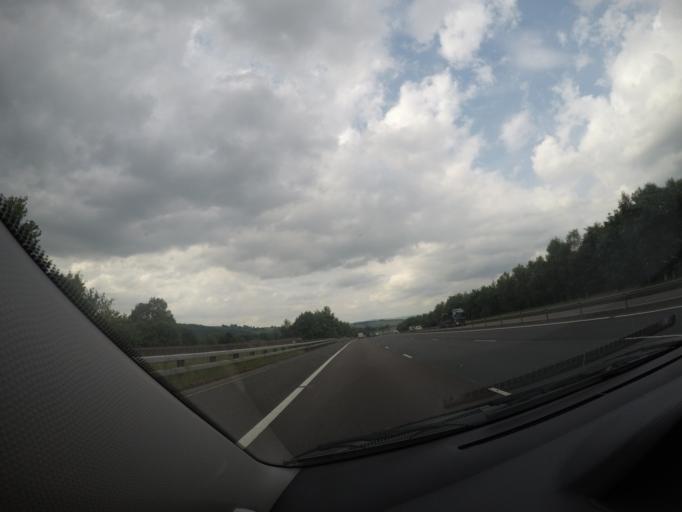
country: GB
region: Scotland
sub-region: Dumfries and Galloway
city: Moffat
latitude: 55.2918
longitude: -3.4393
